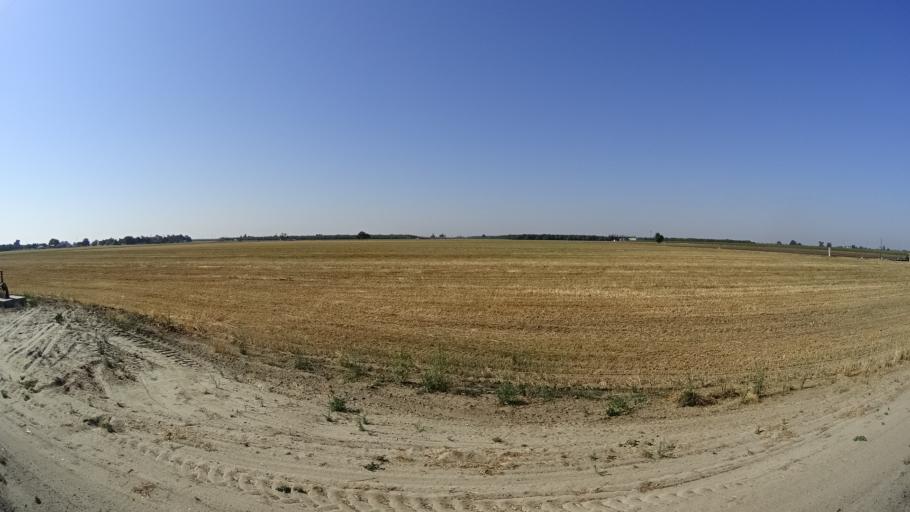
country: US
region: California
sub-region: Kings County
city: Lucerne
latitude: 36.3865
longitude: -119.6157
